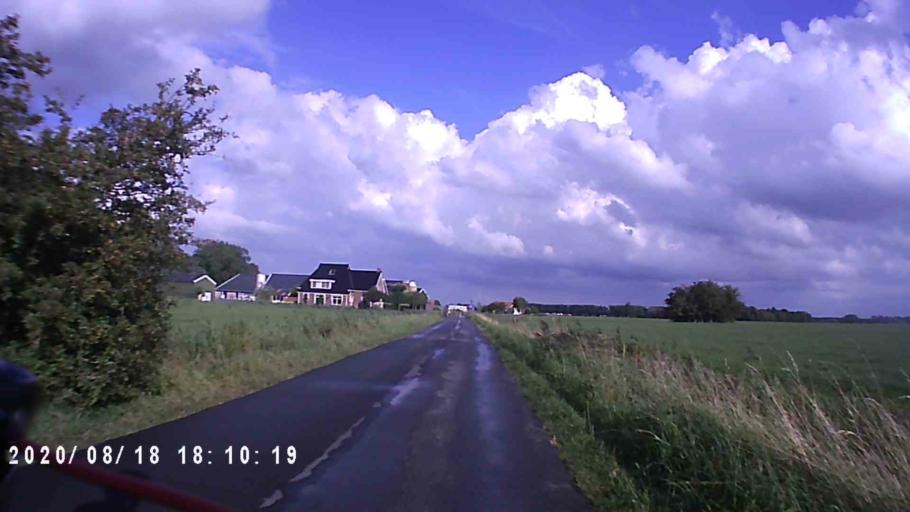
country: NL
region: Groningen
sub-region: Gemeente Zuidhorn
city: Noordhorn
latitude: 53.2810
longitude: 6.4089
